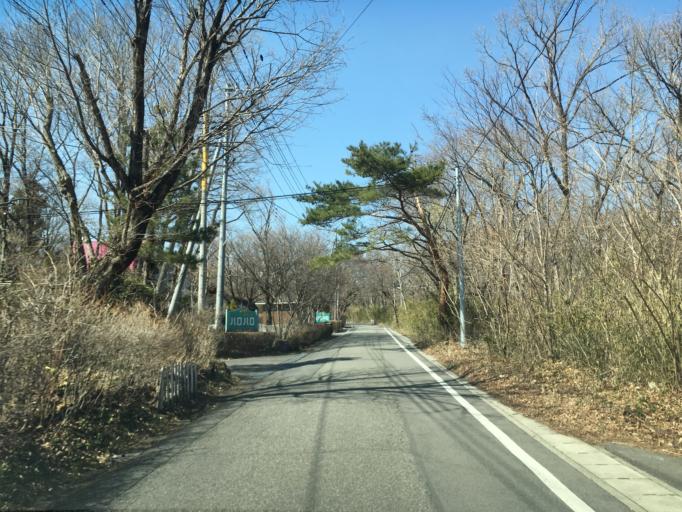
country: JP
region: Tochigi
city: Kuroiso
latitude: 37.0648
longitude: 140.0045
